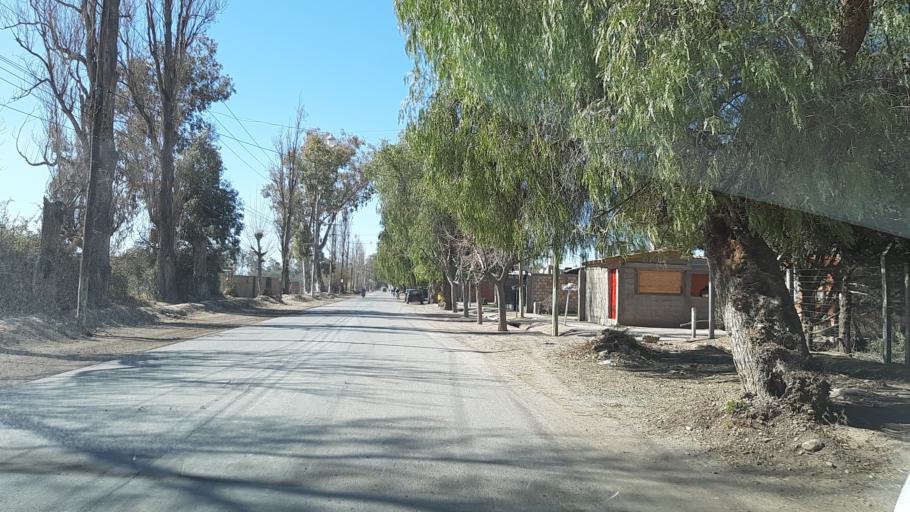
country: AR
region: San Juan
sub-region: Departamento de Zonda
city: Zonda
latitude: -31.4695
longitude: -68.7463
